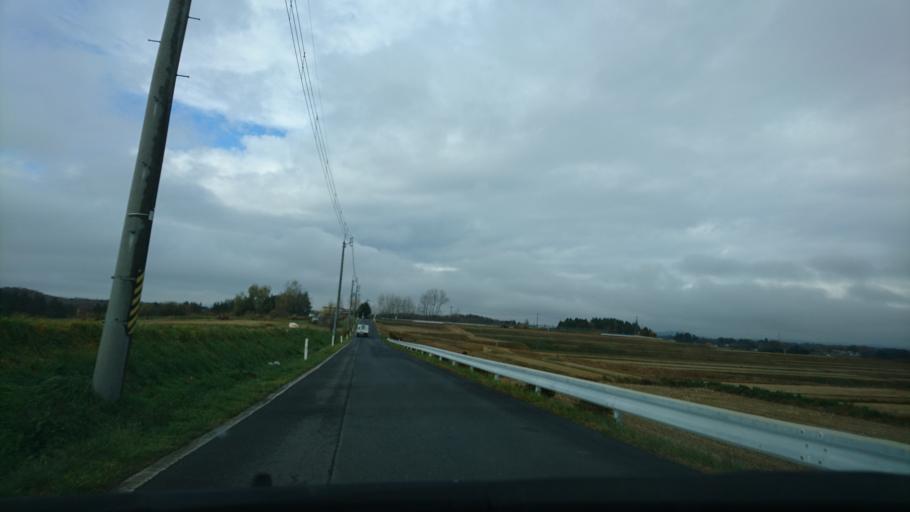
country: JP
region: Iwate
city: Ichinoseki
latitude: 38.8862
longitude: 141.1942
